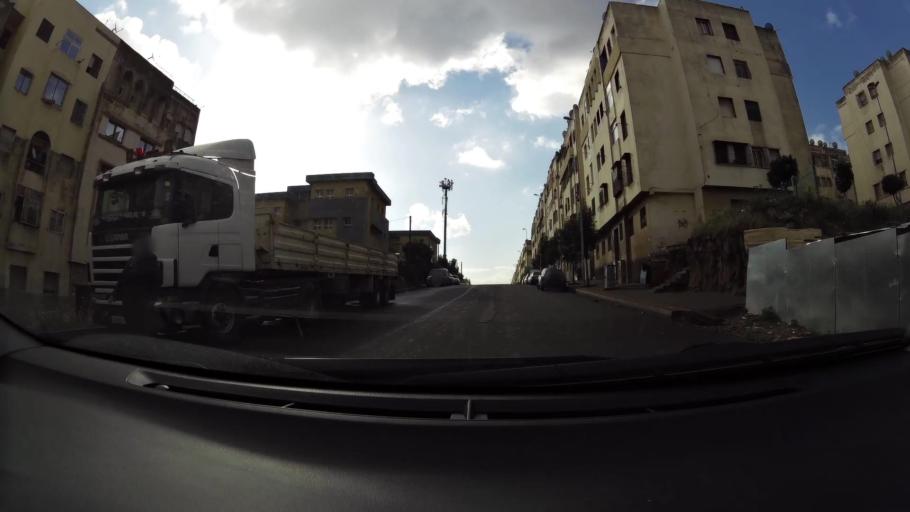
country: MA
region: Grand Casablanca
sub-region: Mediouna
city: Tit Mellil
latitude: 33.5964
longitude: -7.5342
